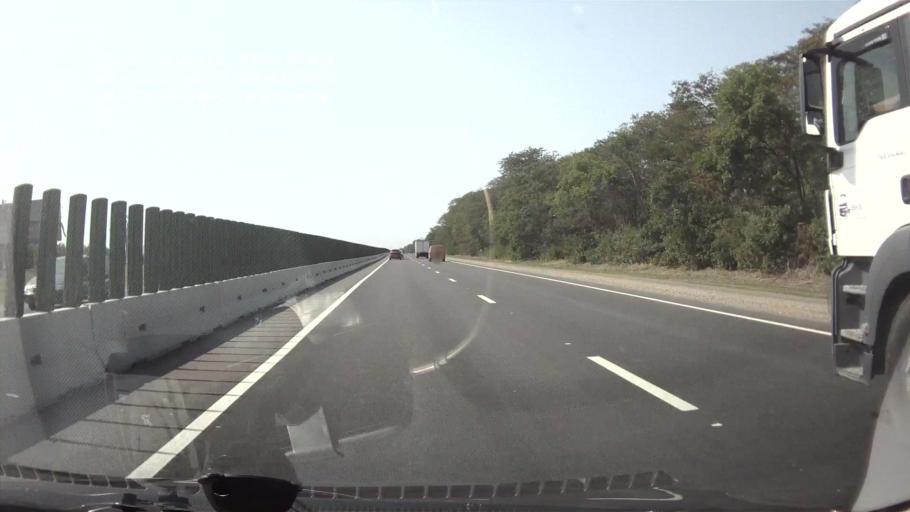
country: RU
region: Adygeya
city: Khatukay
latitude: 45.2206
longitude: 39.6131
